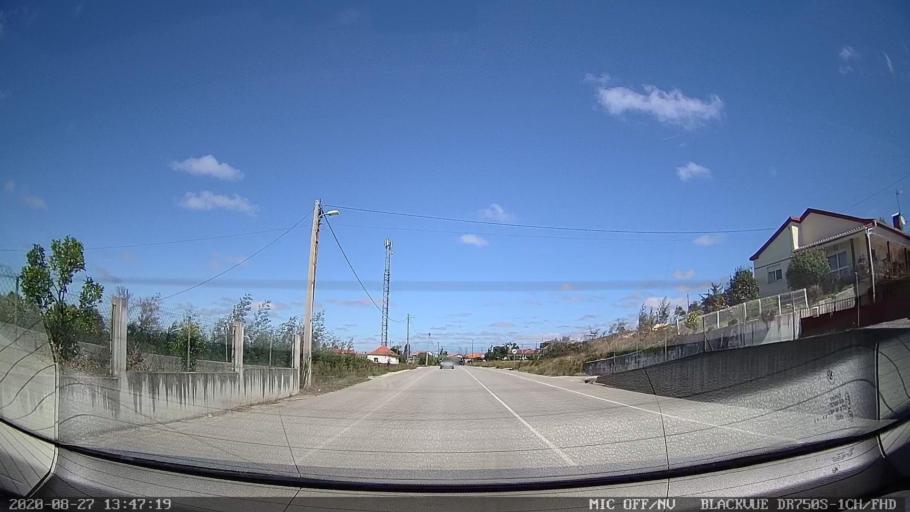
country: PT
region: Coimbra
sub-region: Mira
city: Mira
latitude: 40.3887
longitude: -8.7394
